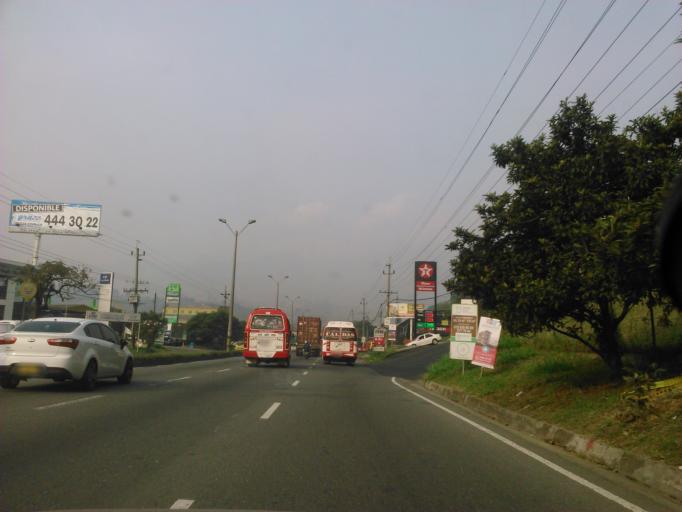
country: CO
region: Antioquia
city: Sabaneta
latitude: 6.1579
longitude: -75.6212
